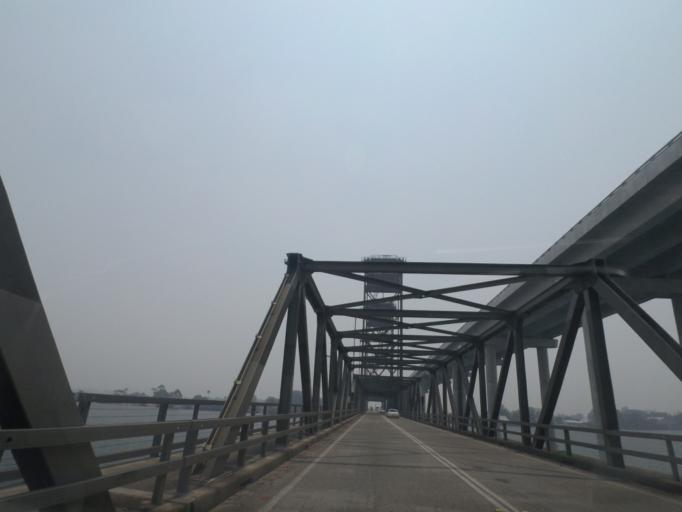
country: AU
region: New South Wales
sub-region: Clarence Valley
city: Maclean
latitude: -29.4310
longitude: 153.2409
